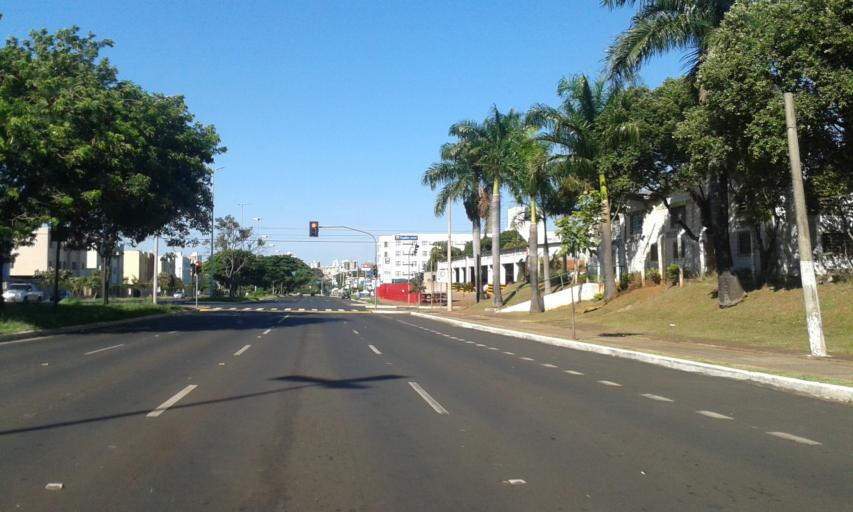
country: BR
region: Minas Gerais
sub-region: Uberlandia
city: Uberlandia
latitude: -18.8990
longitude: -48.2582
